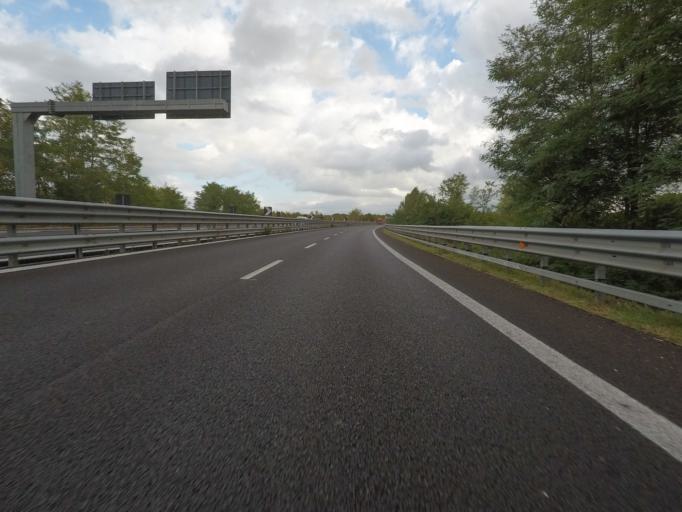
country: IT
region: Tuscany
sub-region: Provincia di Siena
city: Arbia
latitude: 43.3010
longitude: 11.4062
